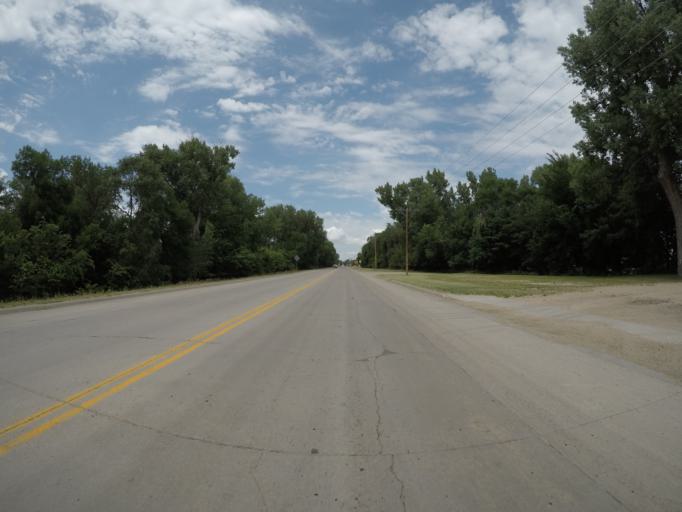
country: US
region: Kansas
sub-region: Rawlins County
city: Atwood
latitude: 39.8080
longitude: -101.0469
